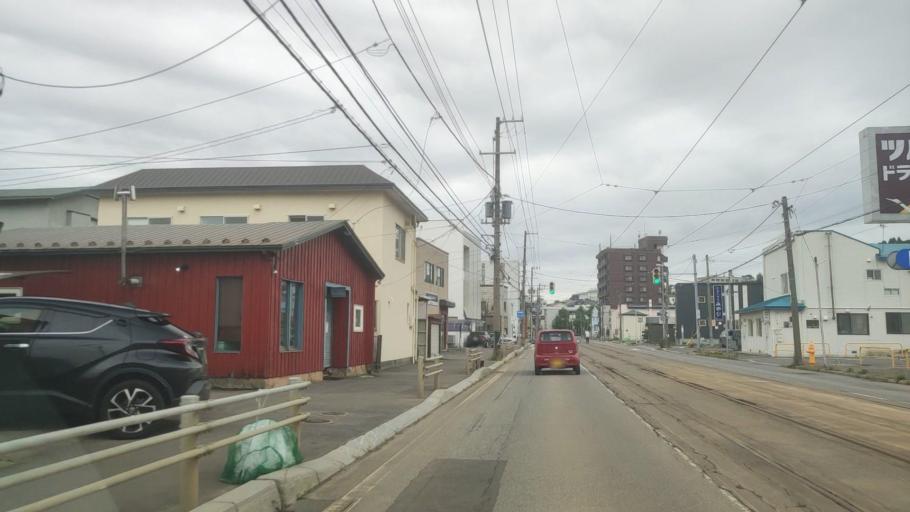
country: JP
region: Hokkaido
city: Hakodate
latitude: 41.7692
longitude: 140.7100
